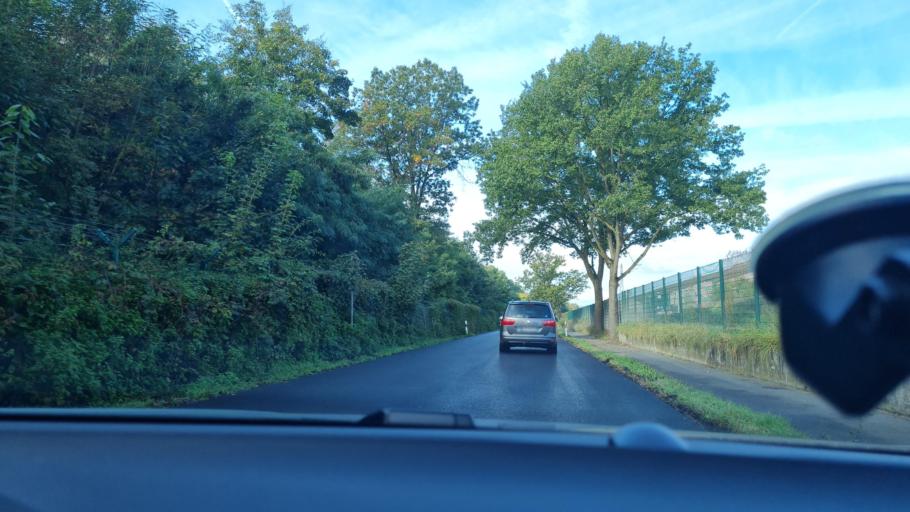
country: DE
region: North Rhine-Westphalia
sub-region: Regierungsbezirk Dusseldorf
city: Dinslaken
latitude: 51.5379
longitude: 6.7651
